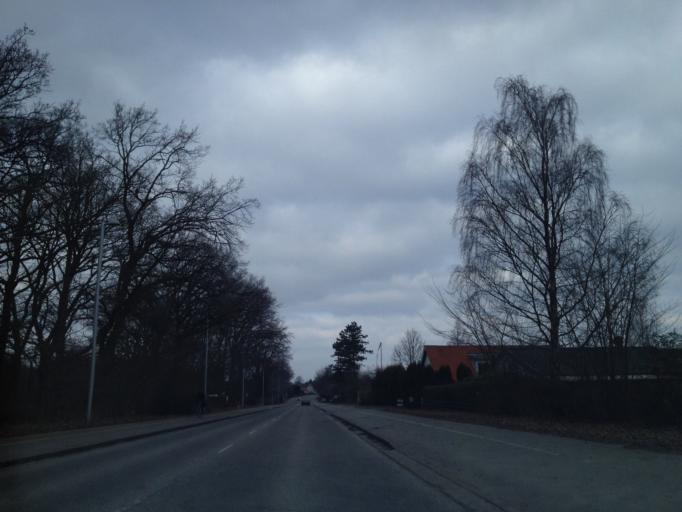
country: DK
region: Capital Region
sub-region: Fredensborg Kommune
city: Humlebaek
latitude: 55.9762
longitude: 12.5439
